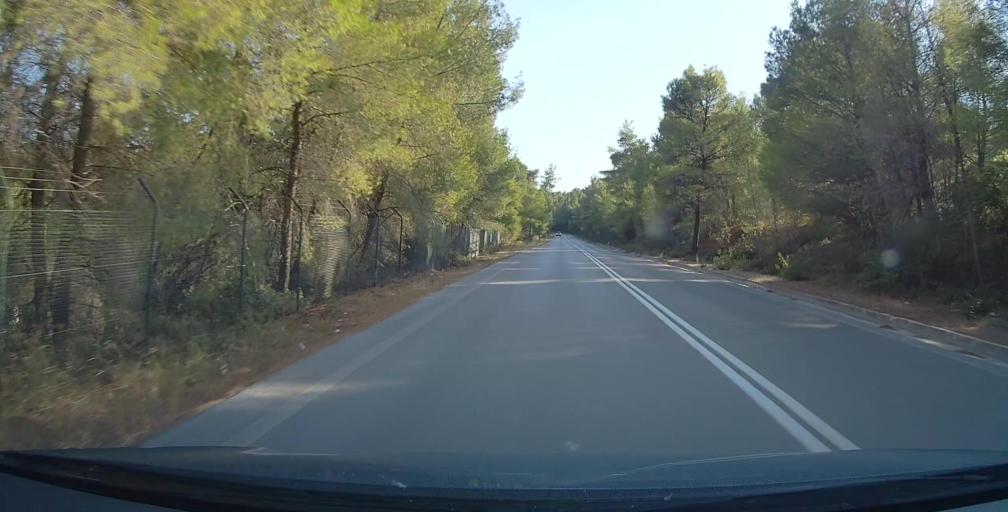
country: GR
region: Central Macedonia
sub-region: Nomos Chalkidikis
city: Neos Marmaras
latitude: 40.0687
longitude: 23.8044
